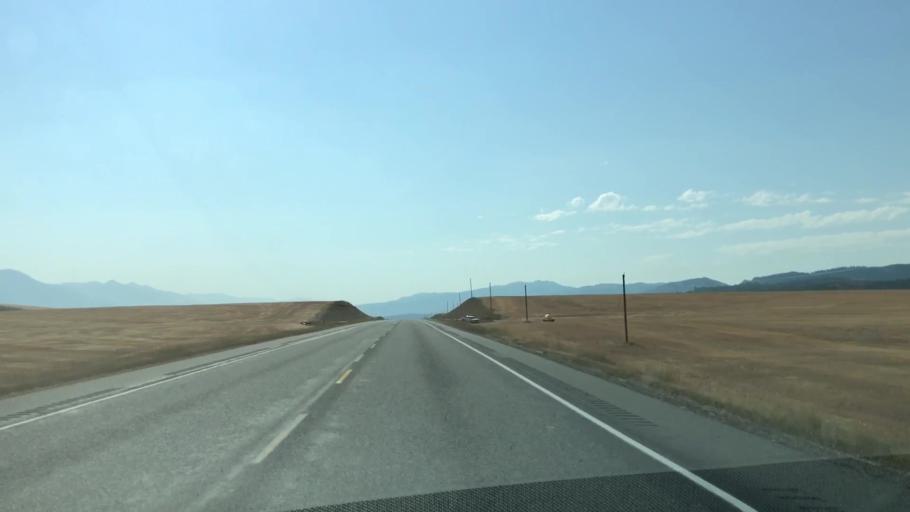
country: US
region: Idaho
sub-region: Teton County
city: Victor
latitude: 43.5125
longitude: -111.4809
